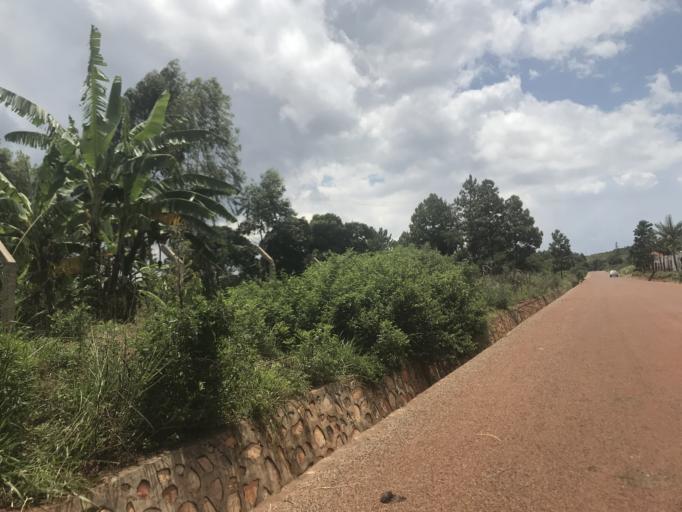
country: UG
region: Eastern Region
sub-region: Jinja District
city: Bugembe
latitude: 0.4893
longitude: 33.2681
